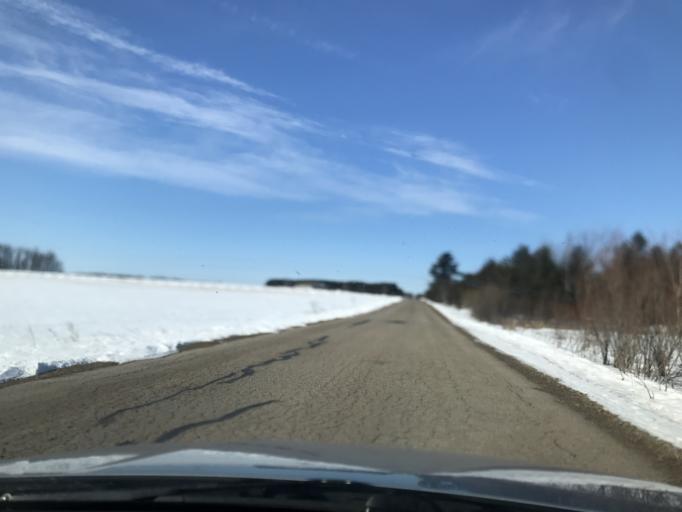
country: US
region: Wisconsin
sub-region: Oconto County
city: Oconto Falls
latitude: 44.9386
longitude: -88.2057
